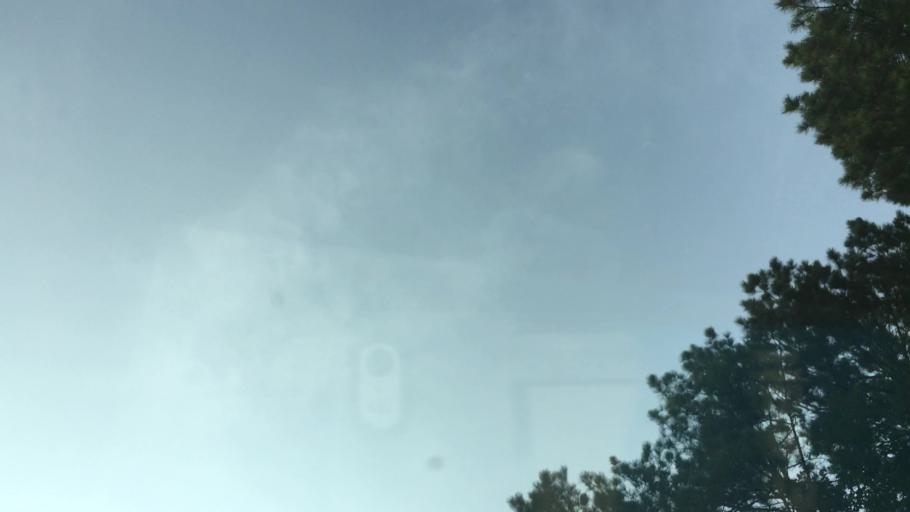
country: US
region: Alabama
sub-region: Tuscaloosa County
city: Lake View
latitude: 33.2194
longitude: -86.9974
